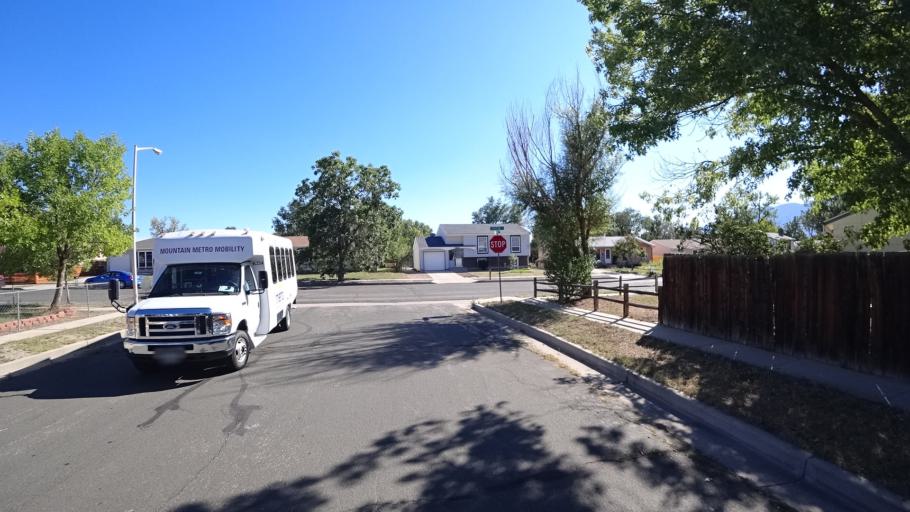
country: US
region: Colorado
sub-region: El Paso County
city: Stratmoor
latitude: 38.7952
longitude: -104.7516
